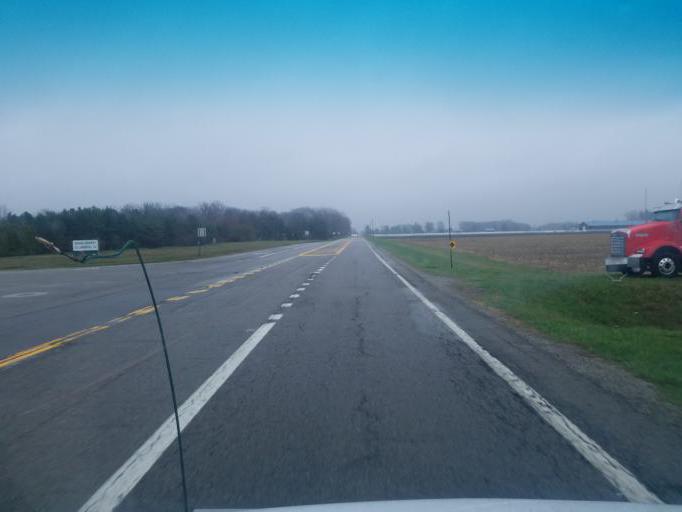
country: US
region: Ohio
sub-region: Wood County
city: Weston
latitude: 41.3722
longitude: -83.7378
